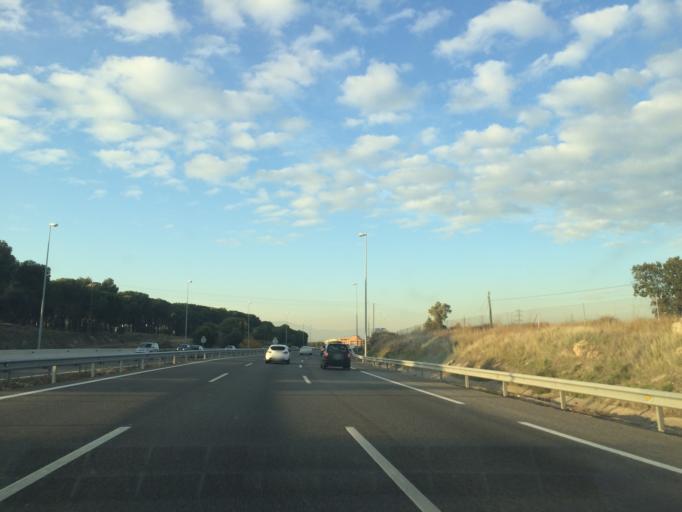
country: ES
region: Madrid
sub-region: Provincia de Madrid
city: Tres Cantos
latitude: 40.5901
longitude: -3.7116
